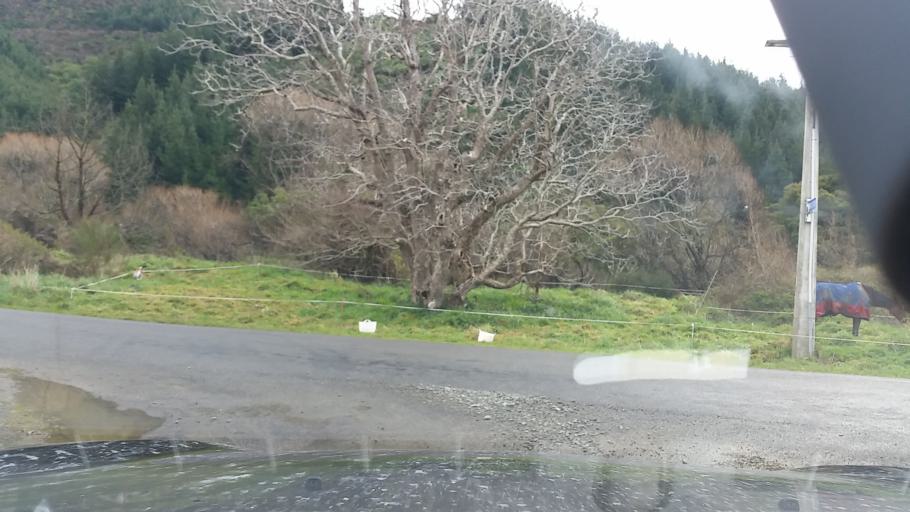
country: NZ
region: Marlborough
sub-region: Marlborough District
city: Picton
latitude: -41.2974
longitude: 173.6656
